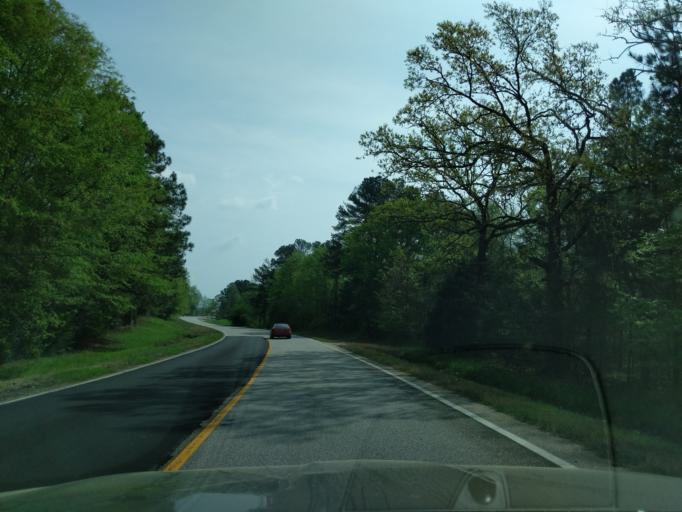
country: US
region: Georgia
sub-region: Lincoln County
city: Lincolnton
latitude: 33.8052
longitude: -82.4003
